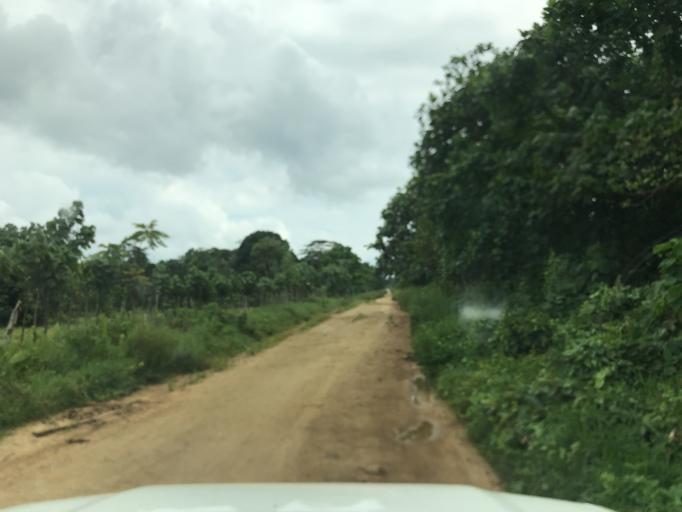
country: VU
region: Sanma
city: Port-Olry
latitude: -15.1850
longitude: 167.0289
